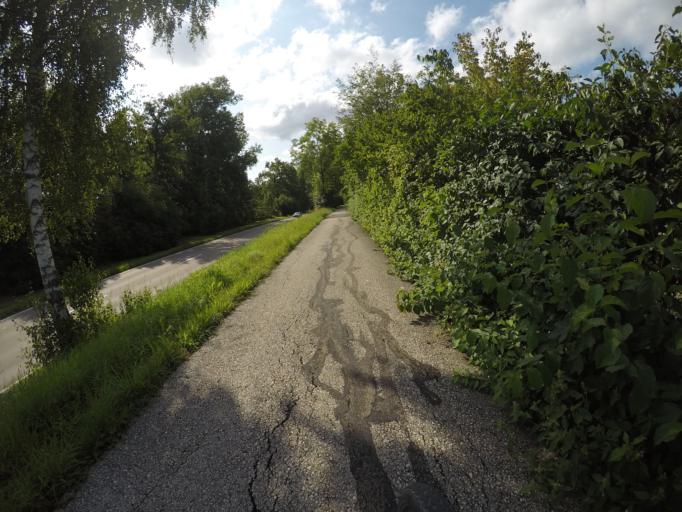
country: DE
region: Baden-Wuerttemberg
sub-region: Regierungsbezirk Stuttgart
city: Unterensingen
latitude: 48.6595
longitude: 9.3631
